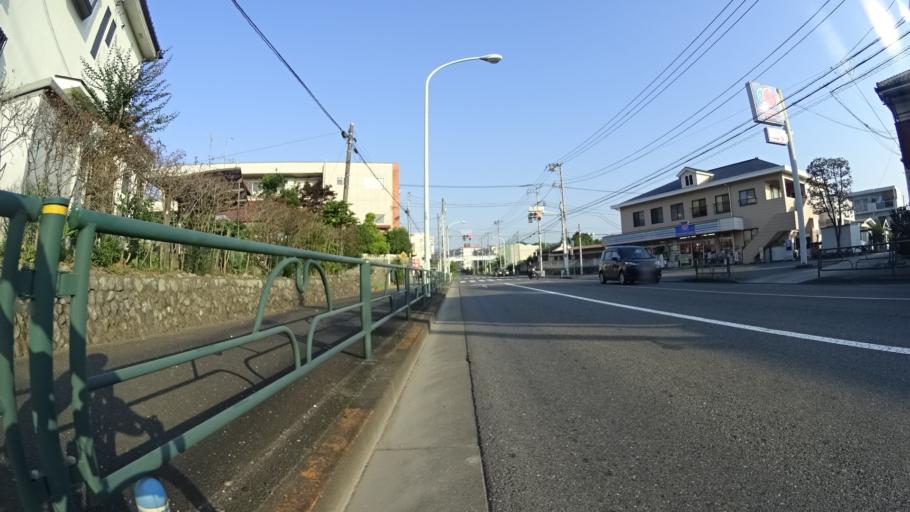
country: JP
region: Tokyo
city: Ome
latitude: 35.7788
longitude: 139.2724
